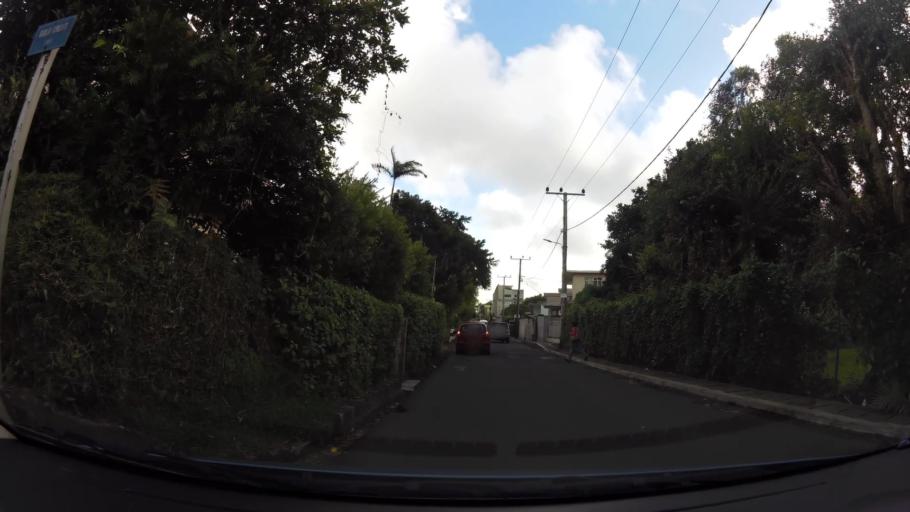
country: MU
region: Plaines Wilhems
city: Curepipe
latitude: -20.3185
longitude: 57.5189
